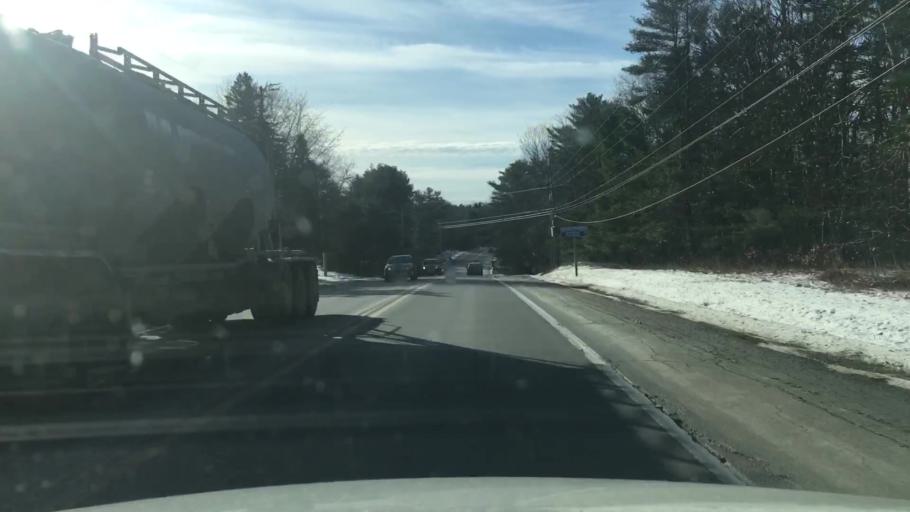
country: US
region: Maine
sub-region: Lincoln County
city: Wiscasset
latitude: 43.9669
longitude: -69.7197
